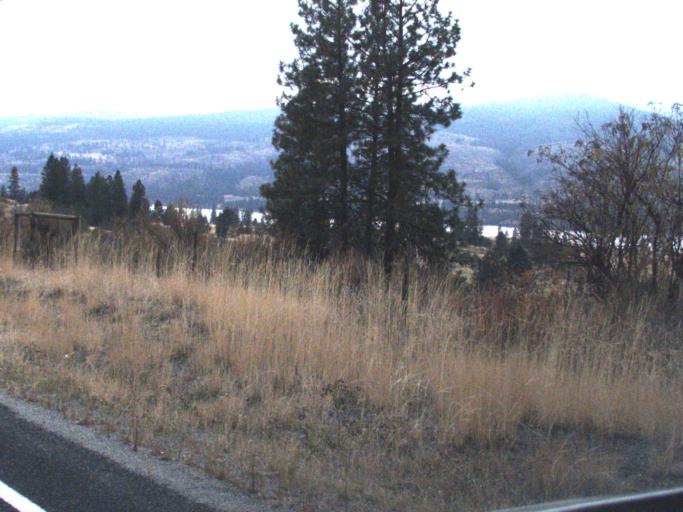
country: US
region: Washington
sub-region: Lincoln County
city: Davenport
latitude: 47.9296
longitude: -118.3214
